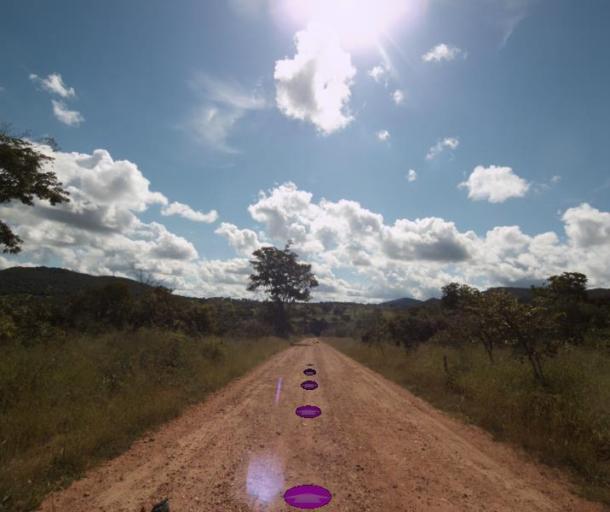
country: BR
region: Goias
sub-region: Jaragua
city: Jaragua
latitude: -15.8236
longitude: -49.1764
